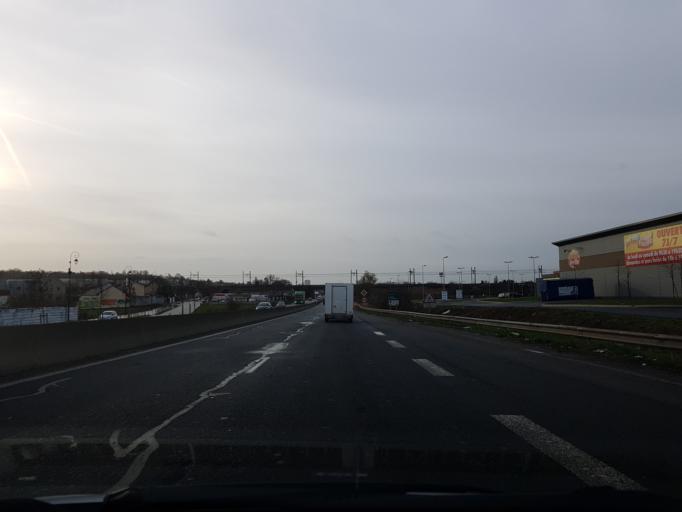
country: FR
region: Ile-de-France
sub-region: Departement de l'Essonne
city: Montgeron
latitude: 48.7174
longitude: 2.4427
